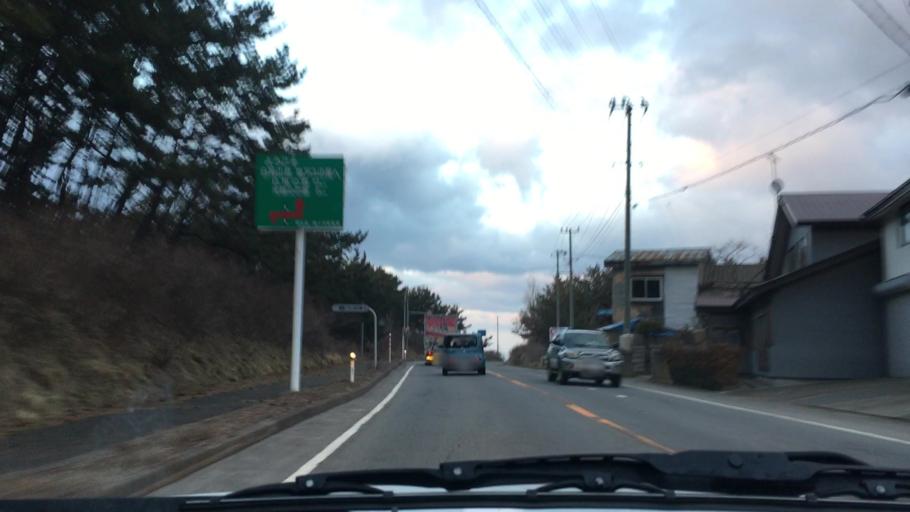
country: JP
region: Aomori
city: Shimokizukuri
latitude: 40.7576
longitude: 140.1546
